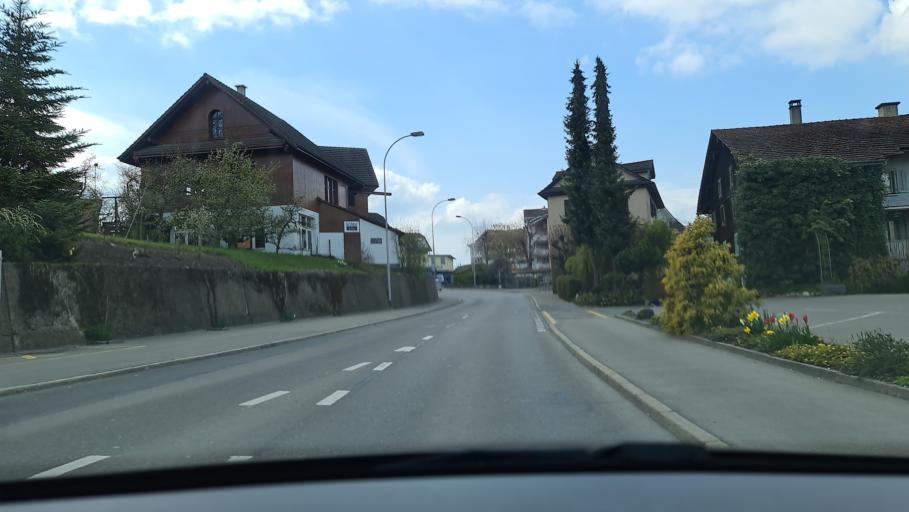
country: CH
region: Lucerne
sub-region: Hochdorf District
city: Ballwil
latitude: 47.1528
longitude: 8.3209
